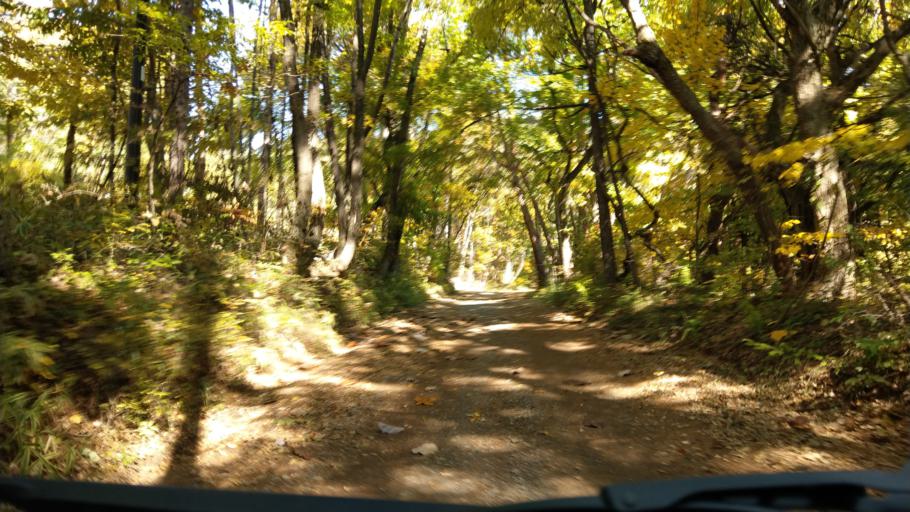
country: JP
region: Nagano
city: Komoro
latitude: 36.3640
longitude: 138.4519
